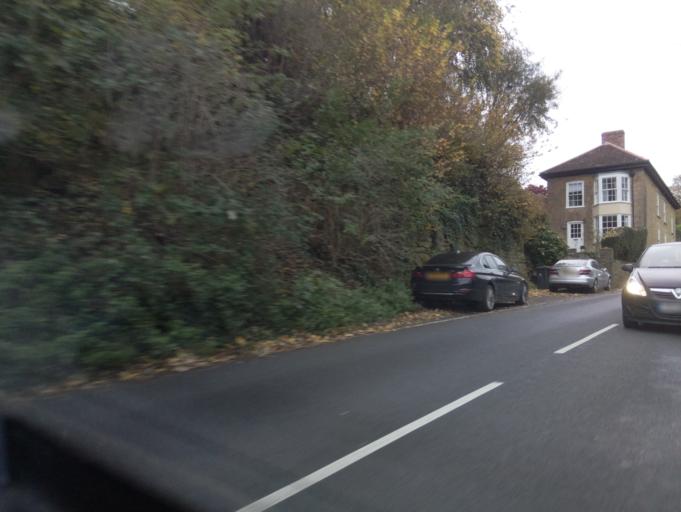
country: GB
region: England
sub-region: Dorset
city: Sherborne
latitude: 50.9516
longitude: -2.5227
